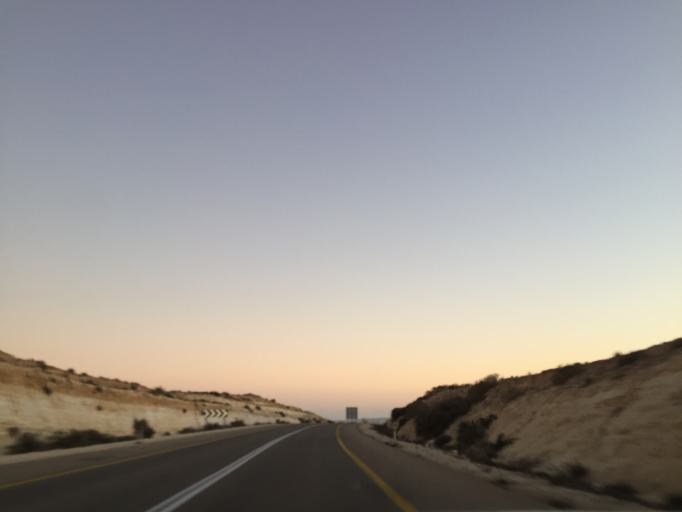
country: IL
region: Southern District
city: Midreshet Ben-Gurion
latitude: 30.8922
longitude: 34.7908
